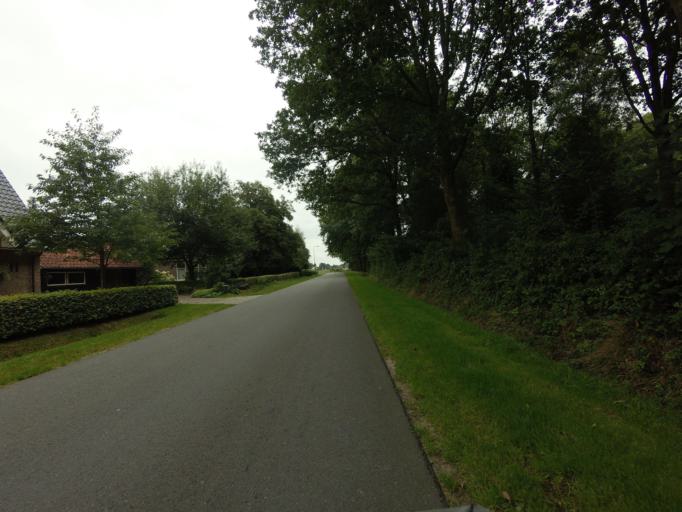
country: NL
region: Overijssel
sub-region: Gemeente Steenwijkerland
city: Steenwijkerwold
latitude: 52.8058
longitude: 6.0718
